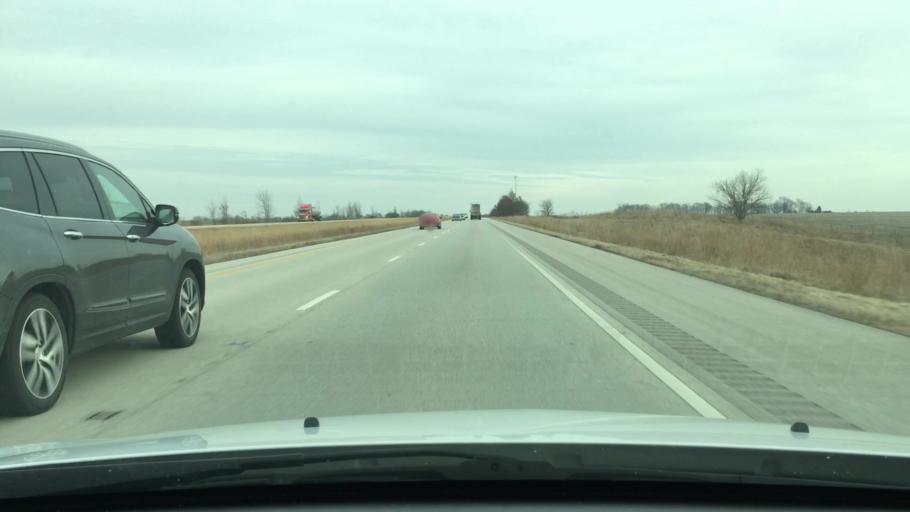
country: US
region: Illinois
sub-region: Sangamon County
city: New Berlin
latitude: 39.7404
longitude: -89.8861
